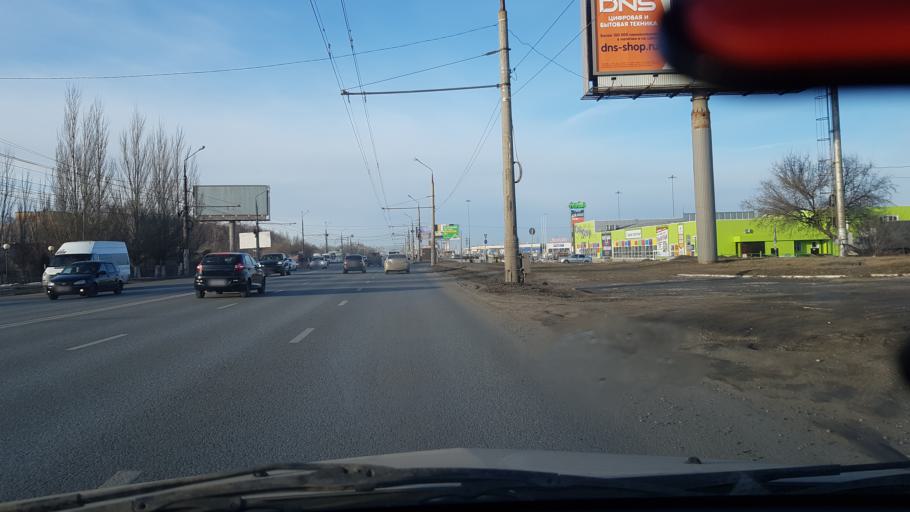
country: RU
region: Samara
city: Tol'yatti
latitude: 53.5380
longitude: 49.3911
